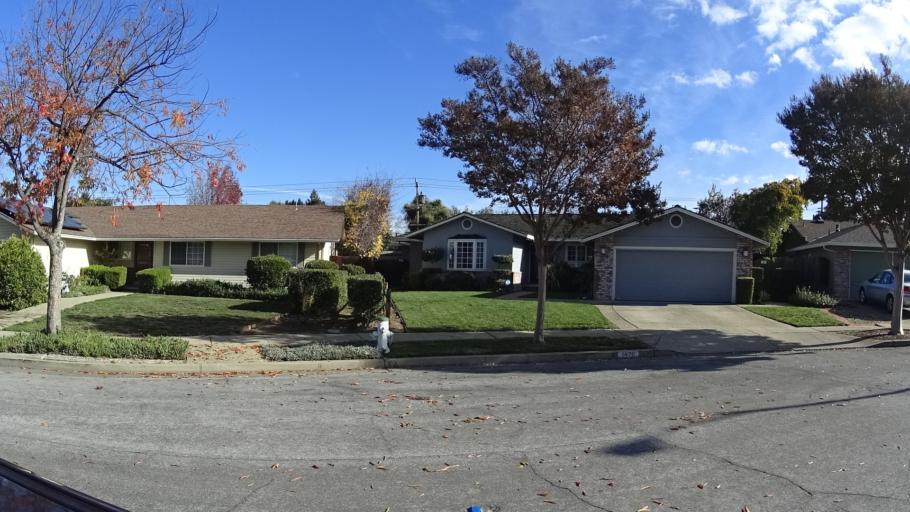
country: US
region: California
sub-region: Santa Clara County
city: Sunnyvale
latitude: 37.3457
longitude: -122.0465
